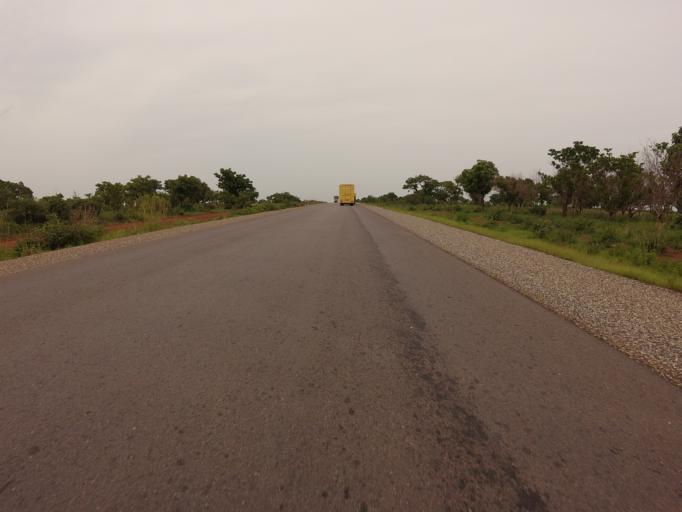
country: GH
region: Northern
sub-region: Yendi
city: Yendi
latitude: 9.3143
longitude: 0.0149
